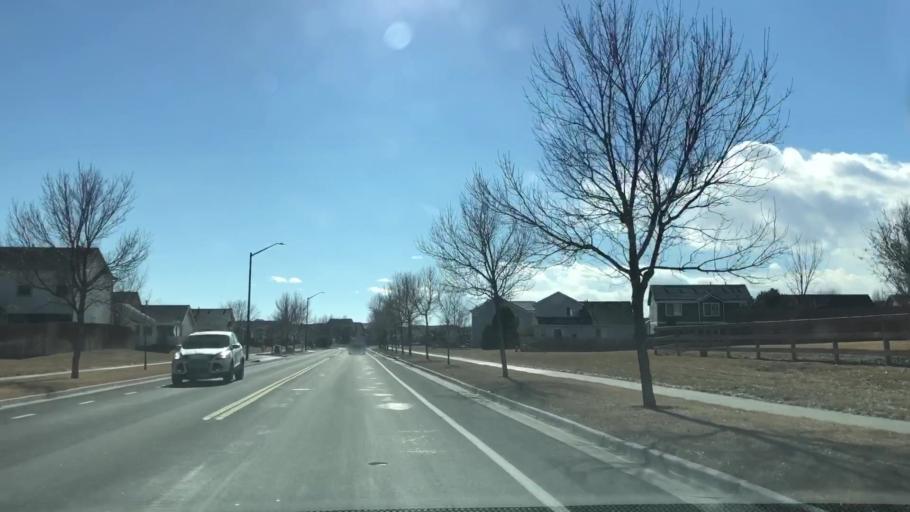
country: US
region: Colorado
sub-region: Larimer County
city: Fort Collins
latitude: 40.6009
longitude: -105.0039
